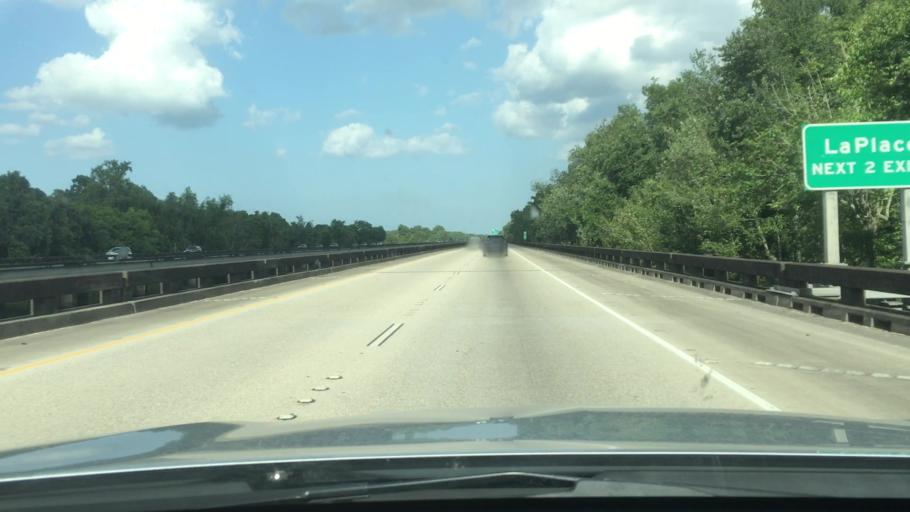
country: US
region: Louisiana
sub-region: Saint John the Baptist Parish
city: Montegut
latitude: 30.1095
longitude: -90.5306
